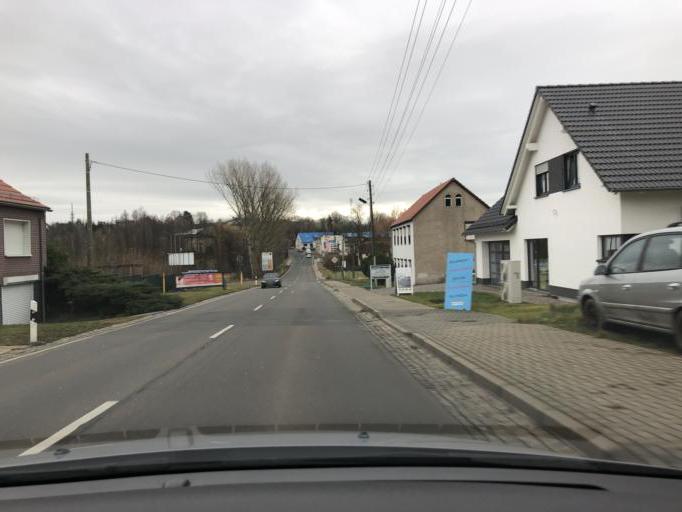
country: DE
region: Saxony
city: Dobeln
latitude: 51.1372
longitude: 13.0984
